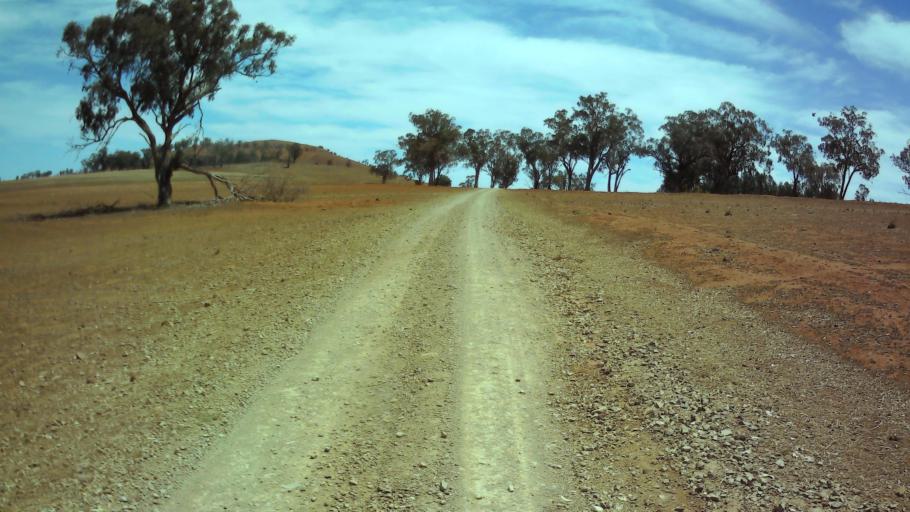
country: AU
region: New South Wales
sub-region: Weddin
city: Grenfell
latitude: -33.7460
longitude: 148.1707
